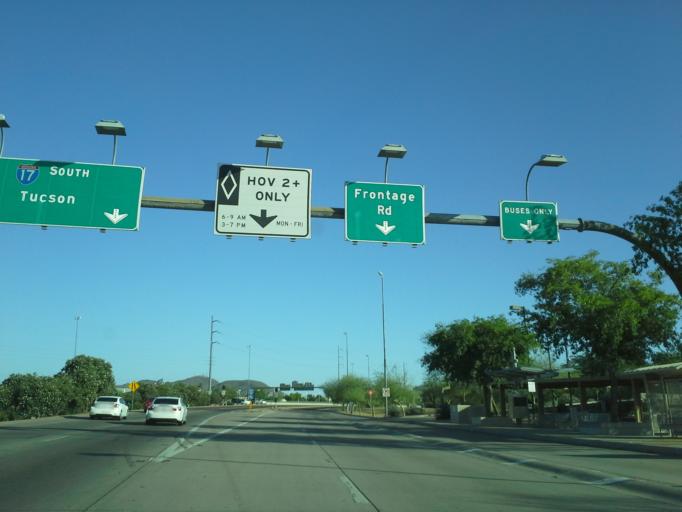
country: US
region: Arizona
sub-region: Maricopa County
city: Glendale
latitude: 33.6389
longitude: -112.1171
